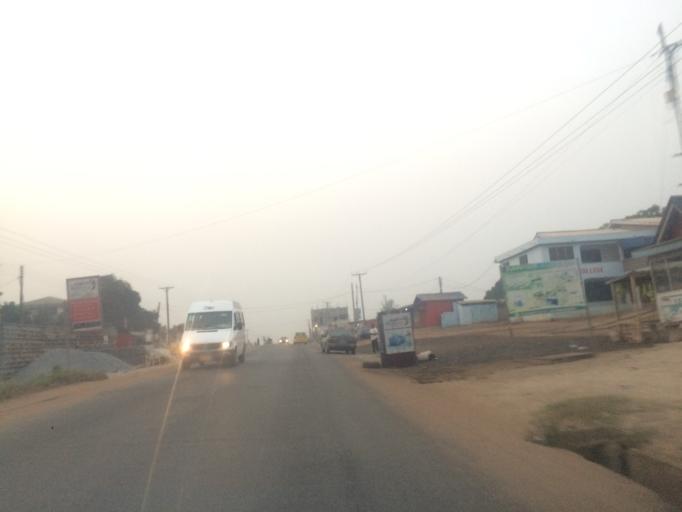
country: GH
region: Greater Accra
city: Teshi Old Town
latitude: 5.5958
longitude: -0.1015
